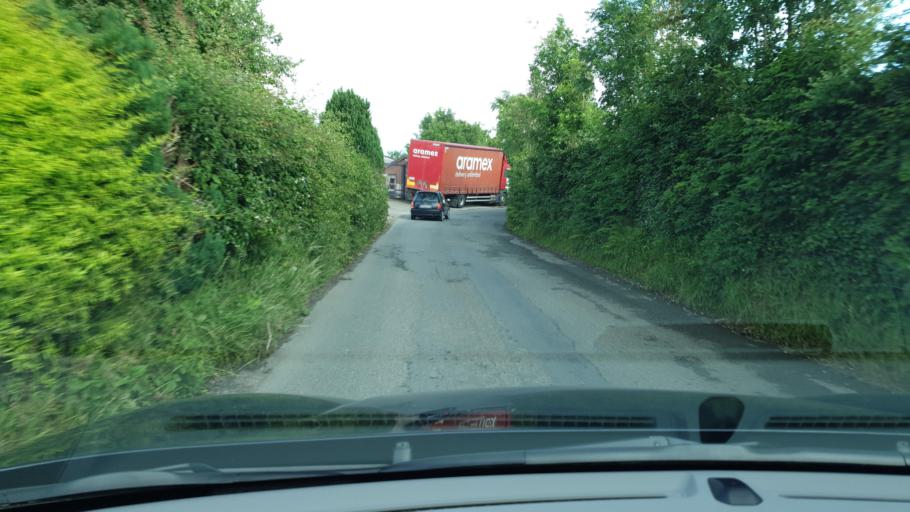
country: IE
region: Leinster
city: Balrothery
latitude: 53.5763
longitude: -6.2003
